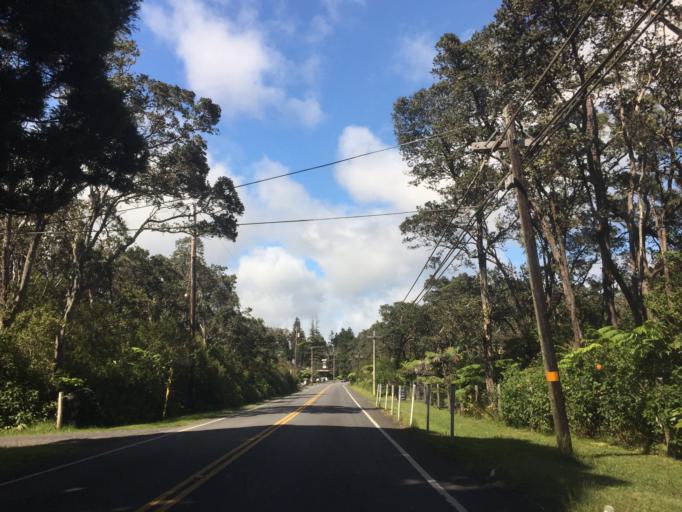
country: US
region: Hawaii
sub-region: Hawaii County
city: Volcano
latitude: 19.4269
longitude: -155.2371
